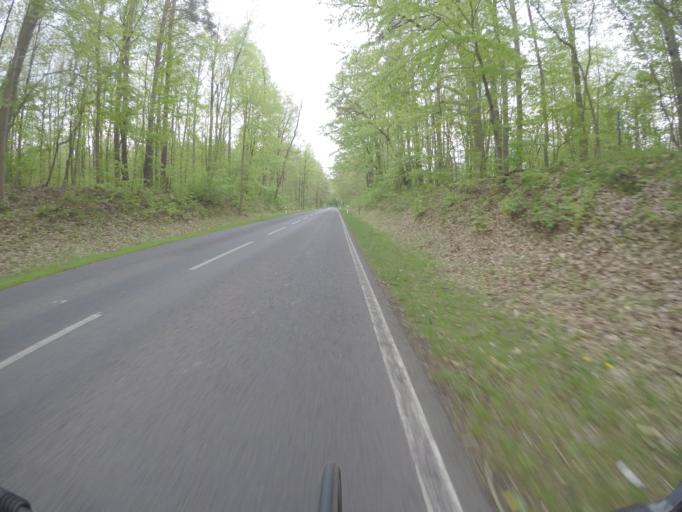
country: DE
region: Brandenburg
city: Joachimsthal
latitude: 52.9223
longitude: 13.7306
